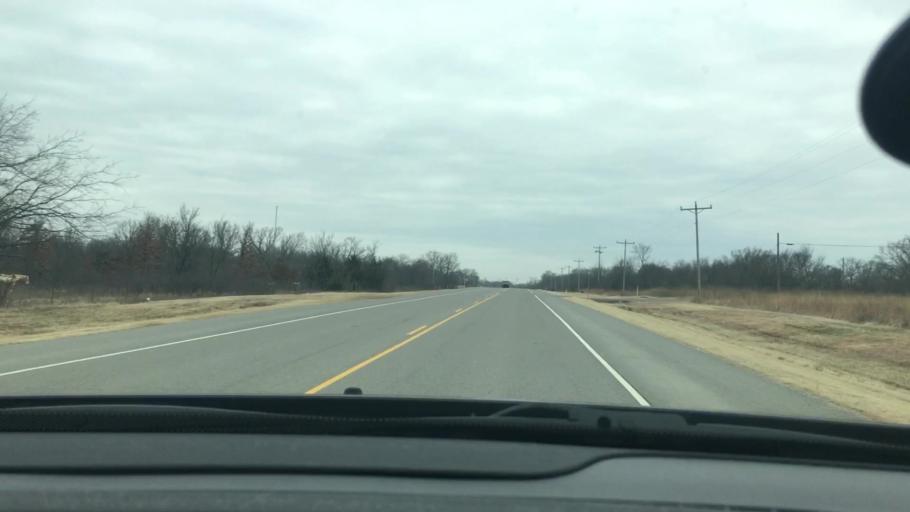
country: US
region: Oklahoma
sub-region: Carter County
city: Healdton
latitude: 34.4799
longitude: -97.4641
